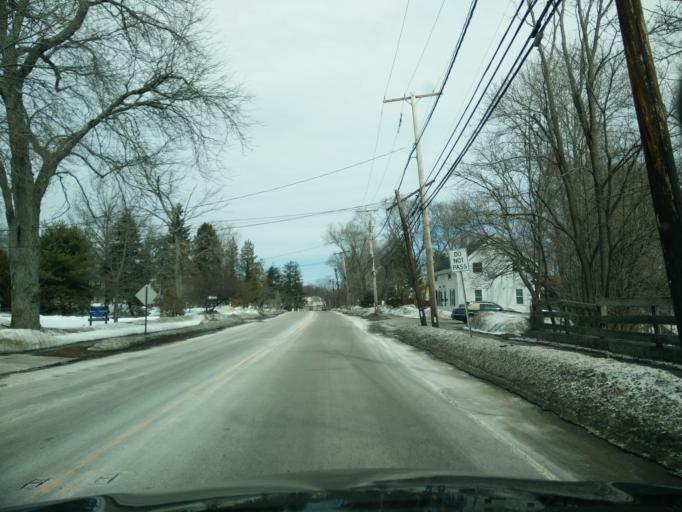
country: US
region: Massachusetts
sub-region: Norfolk County
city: Walpole
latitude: 42.1500
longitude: -71.2500
